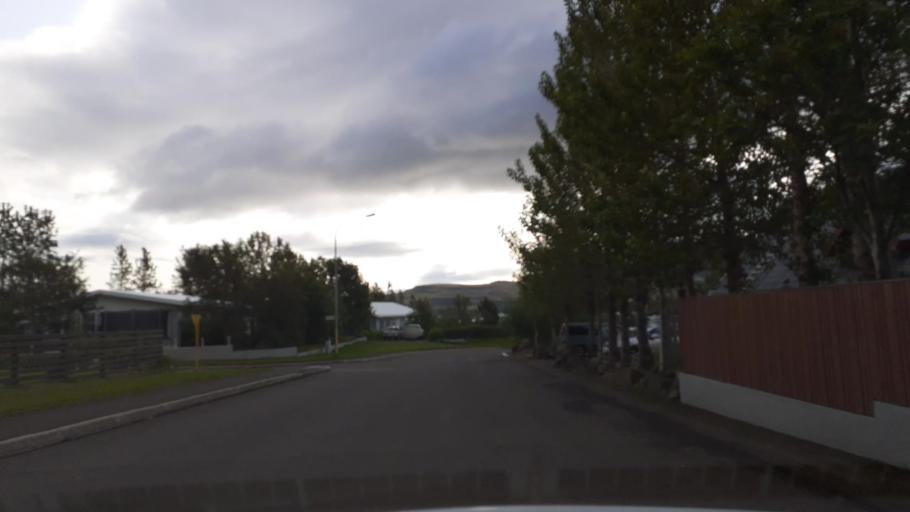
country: IS
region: East
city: Neskaupstadur
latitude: 65.1490
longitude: -13.6718
